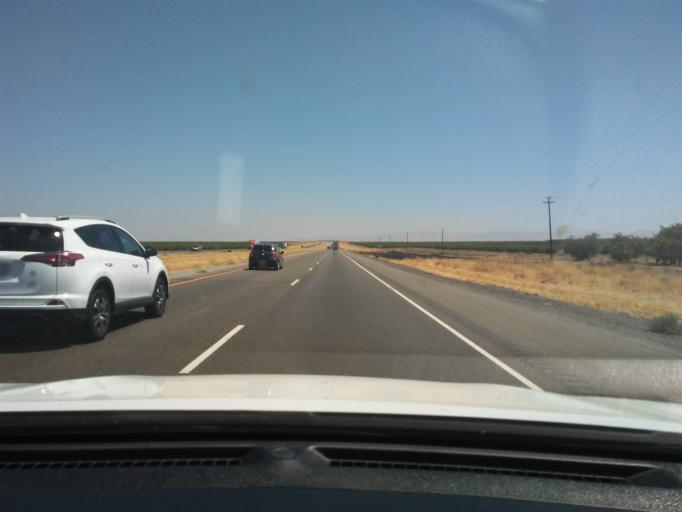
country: US
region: California
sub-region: Merced County
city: South Dos Palos
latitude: 36.7370
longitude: -120.6963
